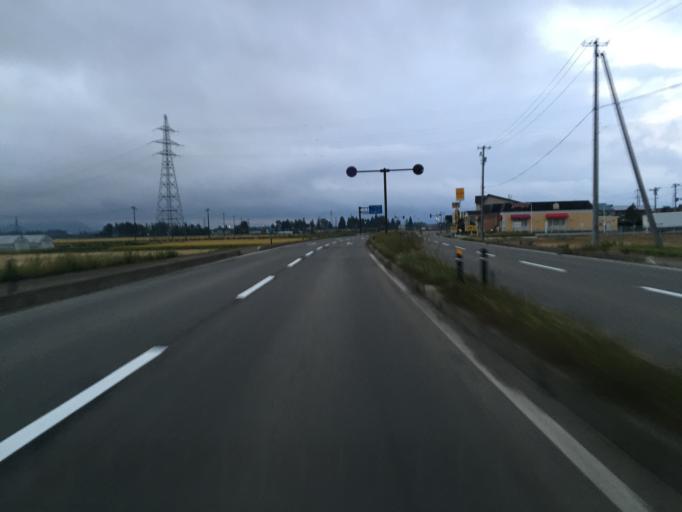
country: JP
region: Fukushima
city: Inawashiro
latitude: 37.5507
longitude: 140.1132
